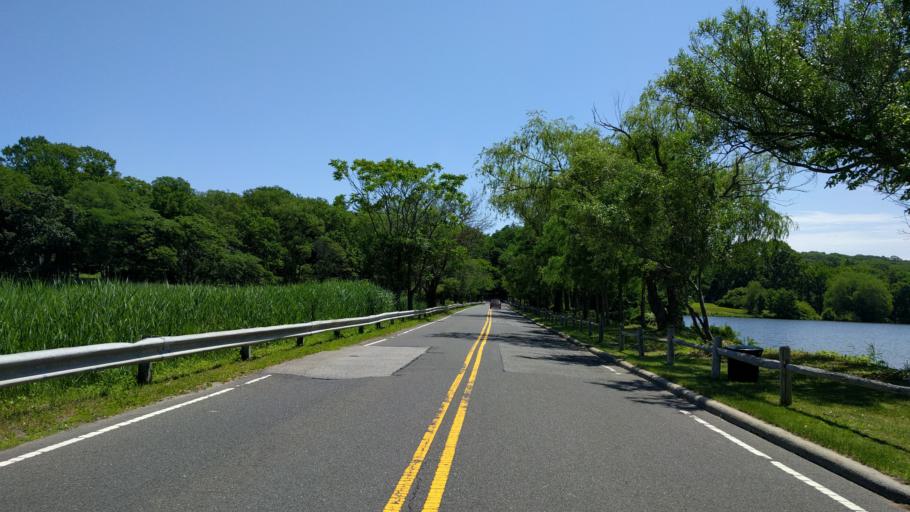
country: US
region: New York
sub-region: Nassau County
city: Bayville
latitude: 40.8879
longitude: -73.5658
